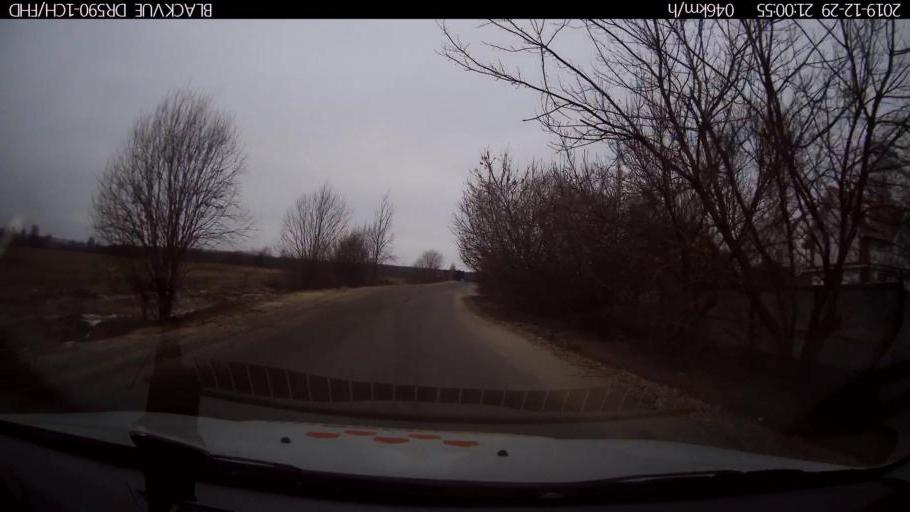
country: RU
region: Nizjnij Novgorod
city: Afonino
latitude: 56.1852
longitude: 43.9900
